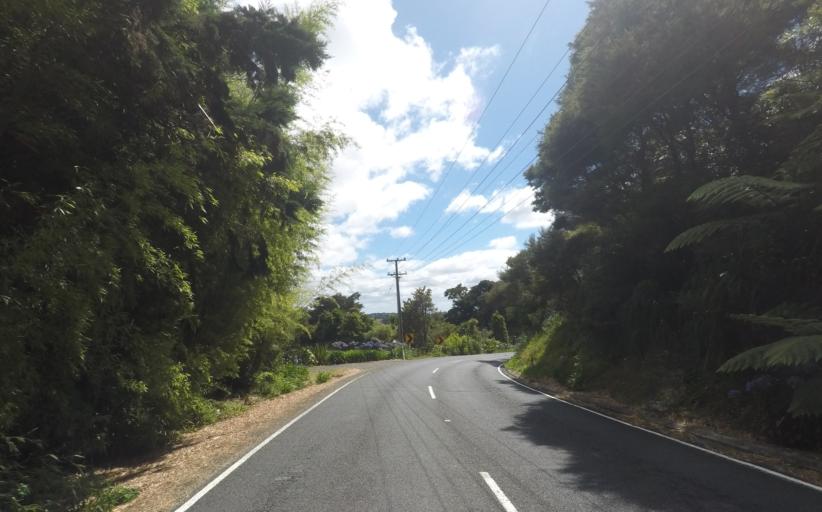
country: NZ
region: Auckland
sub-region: Auckland
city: Muriwai Beach
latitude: -36.8560
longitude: 174.5255
